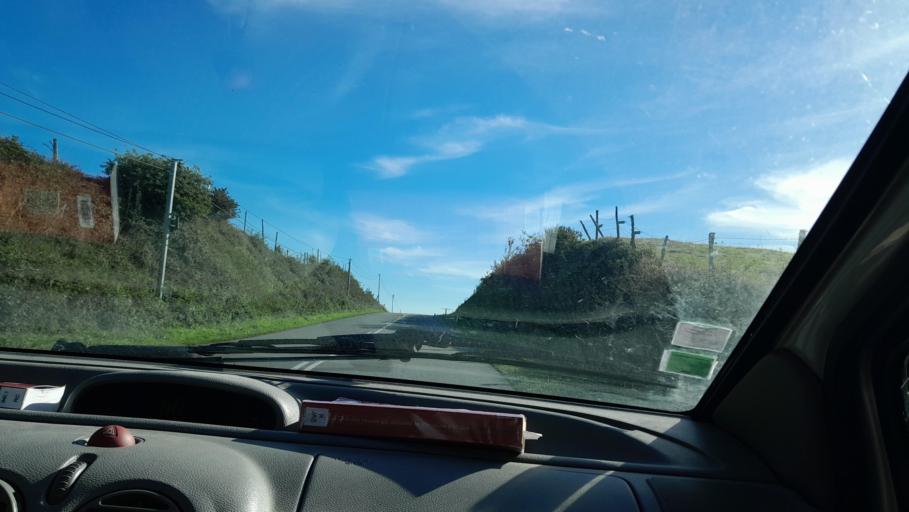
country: FR
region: Brittany
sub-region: Departement d'Ille-et-Vilaine
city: Argentre-du-Plessis
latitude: 47.9840
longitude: -1.1227
